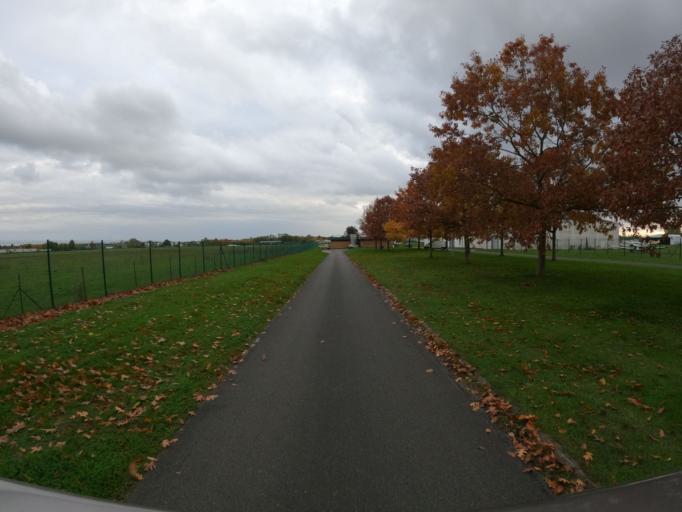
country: FR
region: Ile-de-France
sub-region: Departement de Seine-et-Marne
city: Lognes
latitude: 48.8235
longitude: 2.6293
